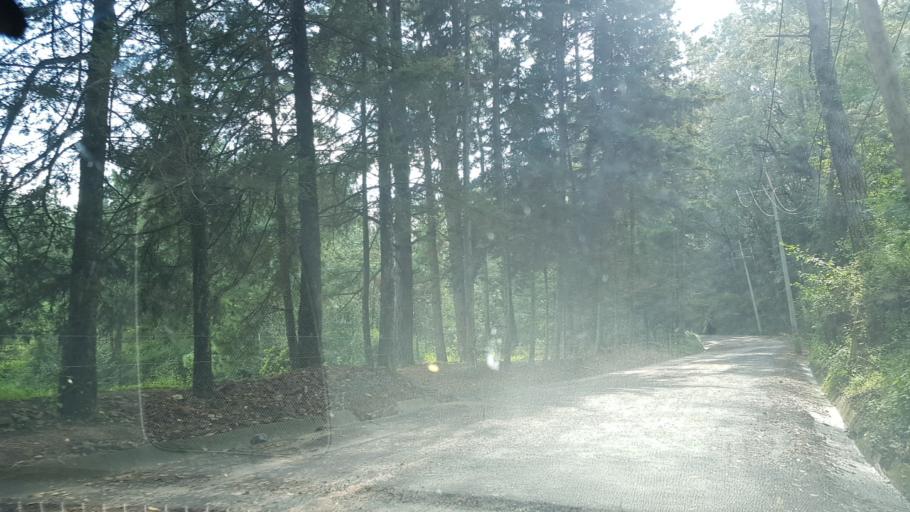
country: MX
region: Mexico
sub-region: Valle de Bravo
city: San Juan Atezcapan
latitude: 19.1424
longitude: -100.1585
